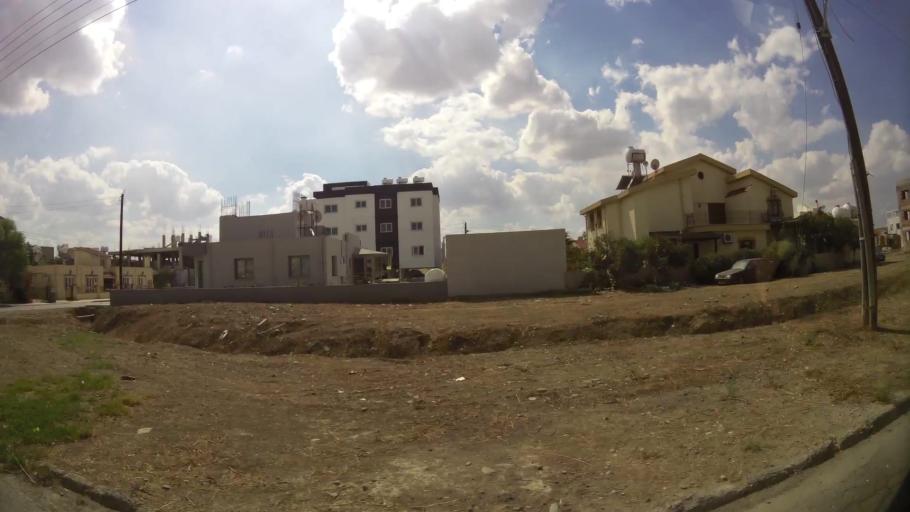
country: CY
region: Lefkosia
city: Nicosia
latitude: 35.2198
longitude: 33.2974
